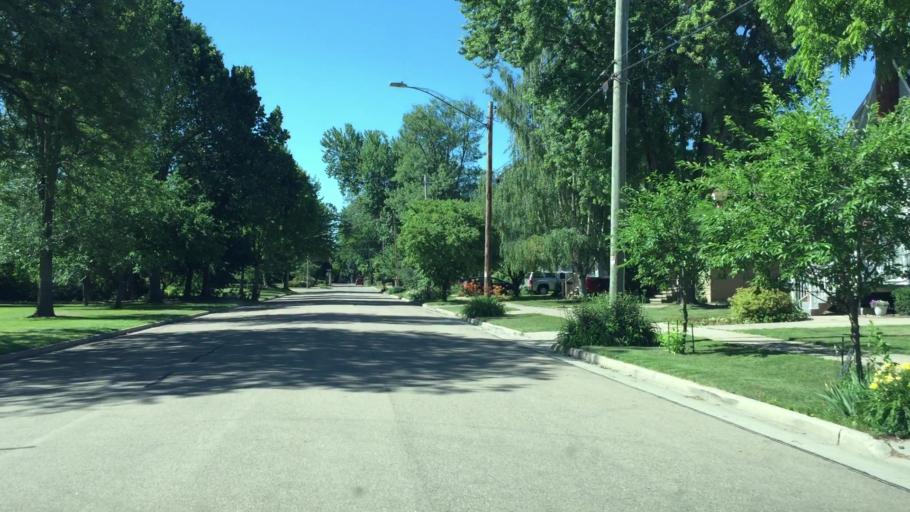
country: US
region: Wisconsin
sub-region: Winnebago County
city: Menasha
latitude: 44.1949
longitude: -88.4421
